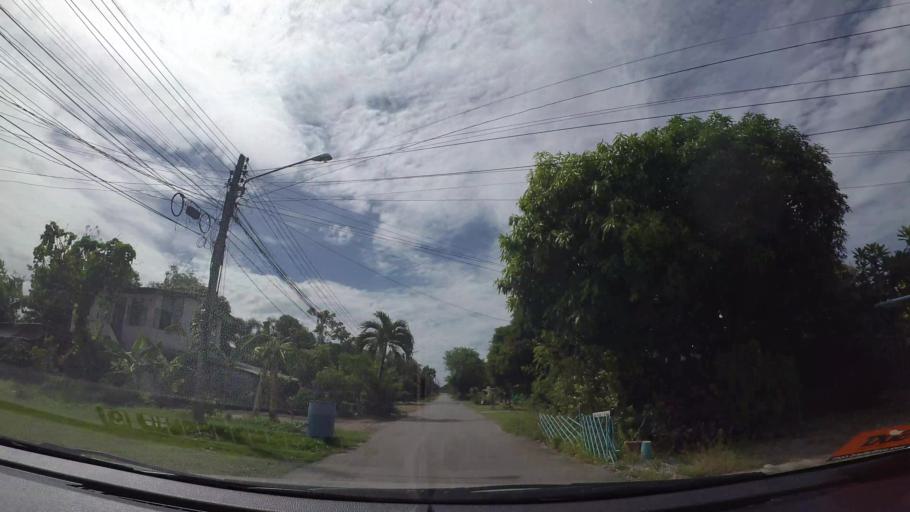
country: TH
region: Chon Buri
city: Sattahip
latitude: 12.6639
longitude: 100.9137
